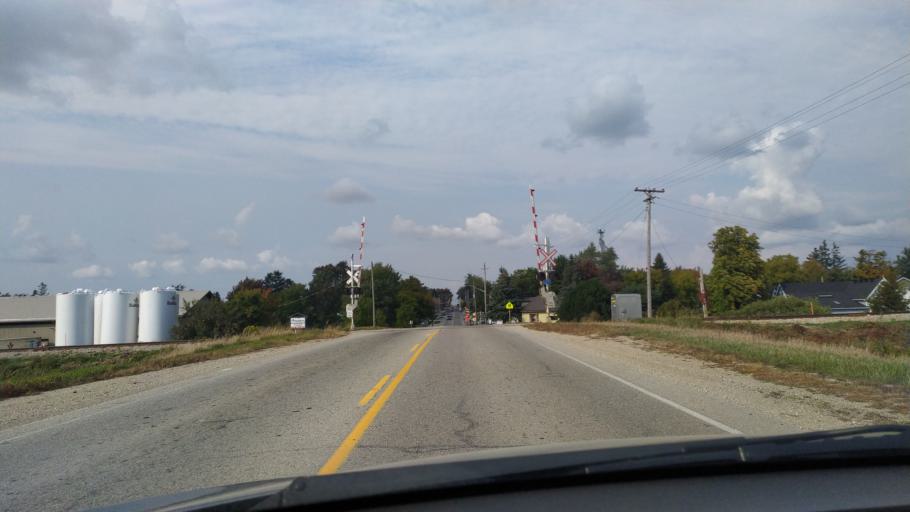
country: CA
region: Ontario
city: Stratford
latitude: 43.3653
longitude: -80.8369
